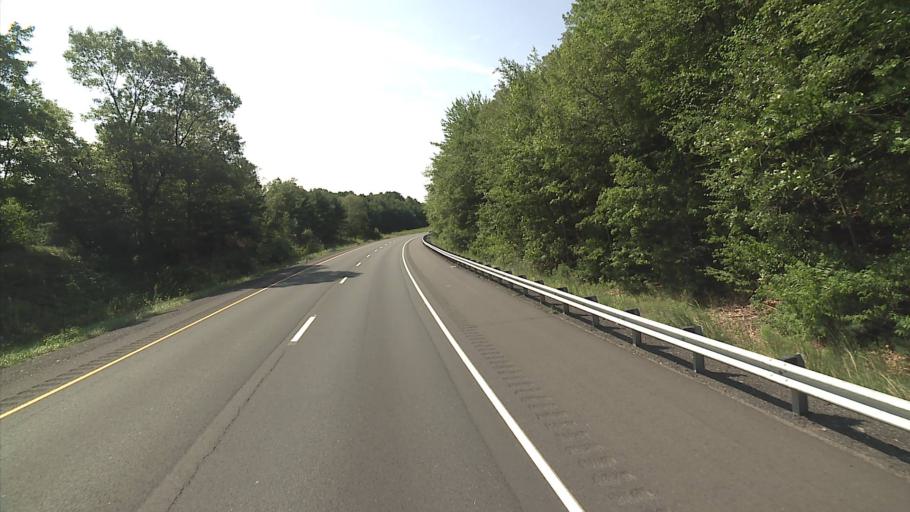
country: US
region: Connecticut
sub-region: Hartford County
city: Glastonbury Center
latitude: 41.6908
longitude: -72.5404
